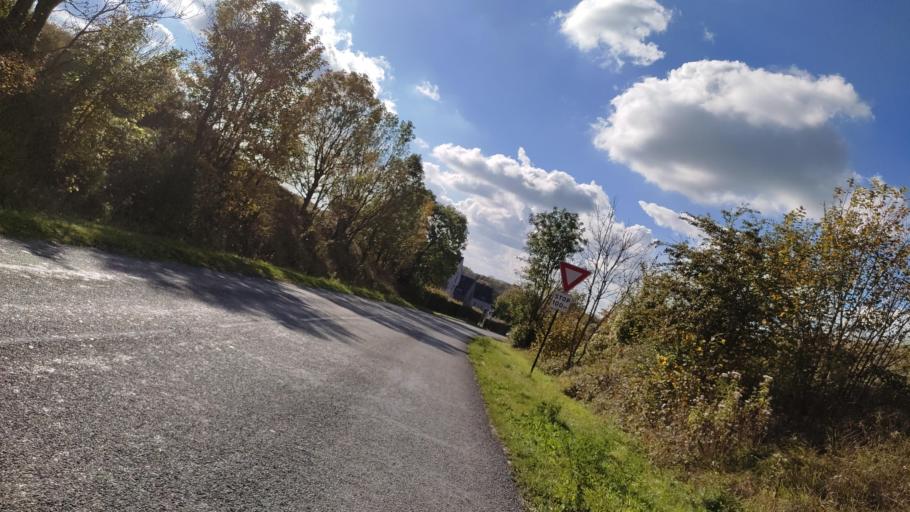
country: FR
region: Nord-Pas-de-Calais
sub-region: Departement du Pas-de-Calais
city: Saint-Laurent-Blangy
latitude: 50.3066
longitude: 2.8230
